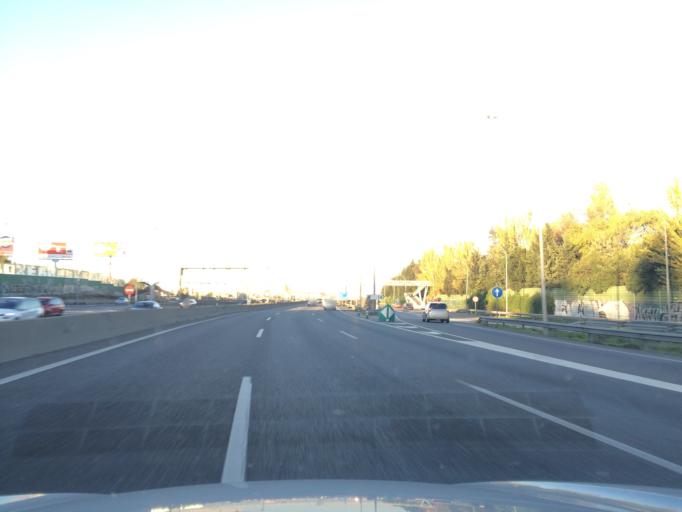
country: ES
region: Madrid
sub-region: Provincia de Madrid
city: Las Tablas
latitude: 40.5205
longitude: -3.6521
